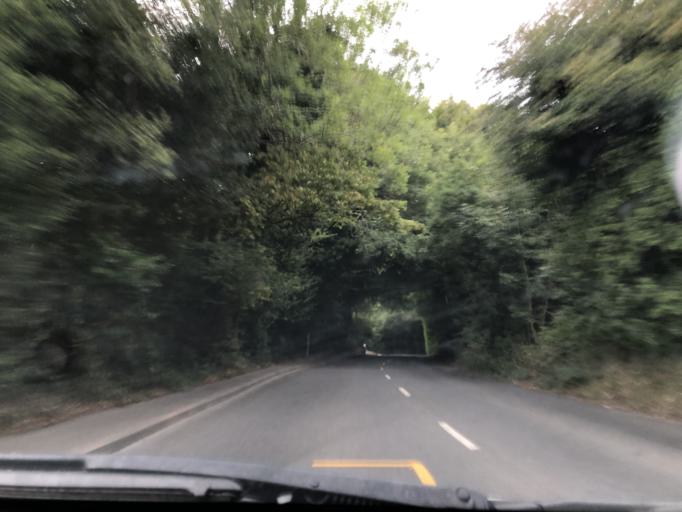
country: GB
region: England
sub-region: Kent
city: Sevenoaks
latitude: 51.2552
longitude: 0.1990
